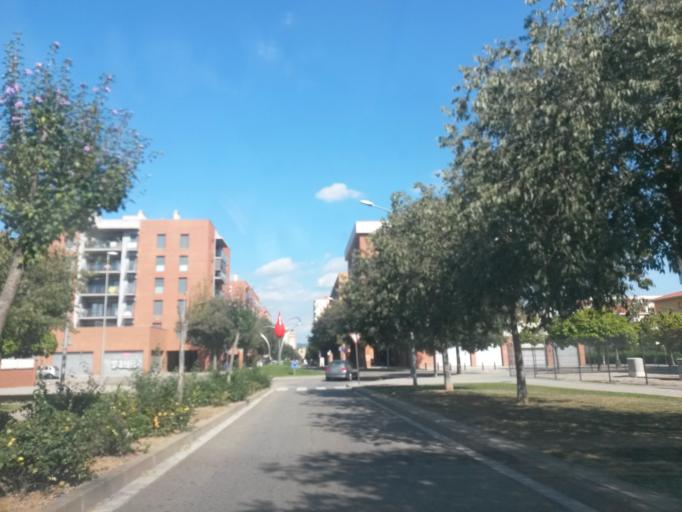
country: ES
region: Catalonia
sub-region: Provincia de Girona
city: Salt
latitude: 41.9689
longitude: 2.7930
